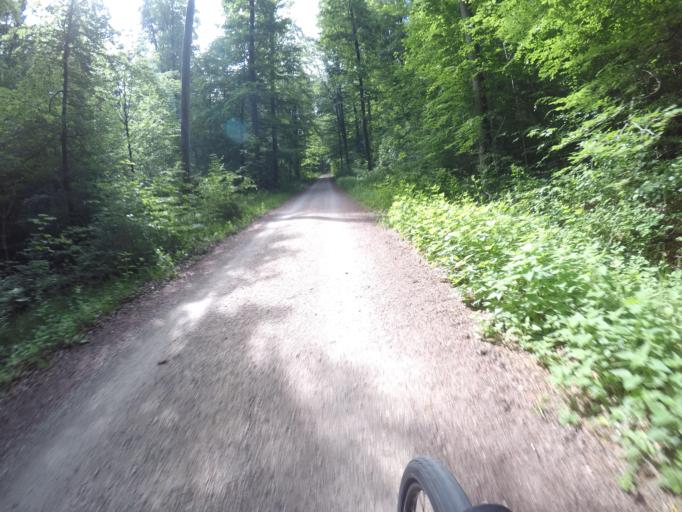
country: DE
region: Baden-Wuerttemberg
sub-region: Regierungsbezirk Stuttgart
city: Denkendorf
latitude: 48.6808
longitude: 9.3177
